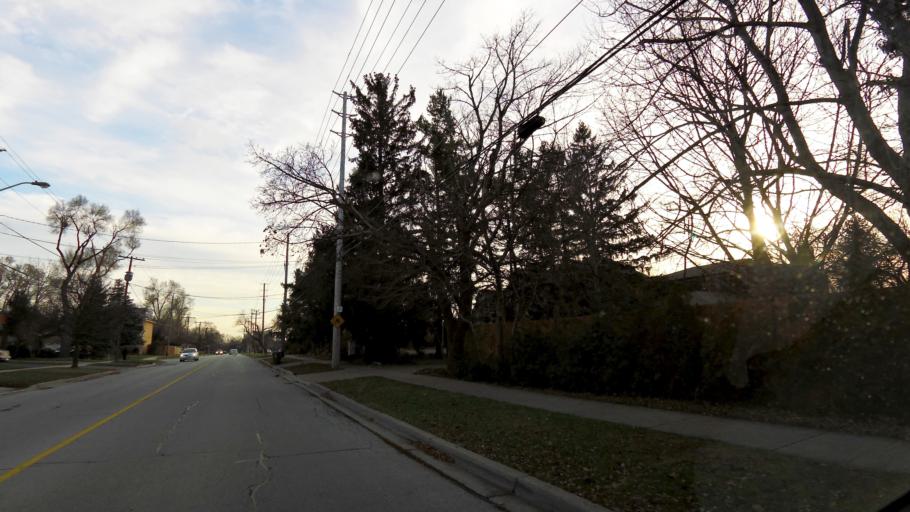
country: CA
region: Ontario
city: Etobicoke
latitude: 43.6321
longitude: -79.5662
